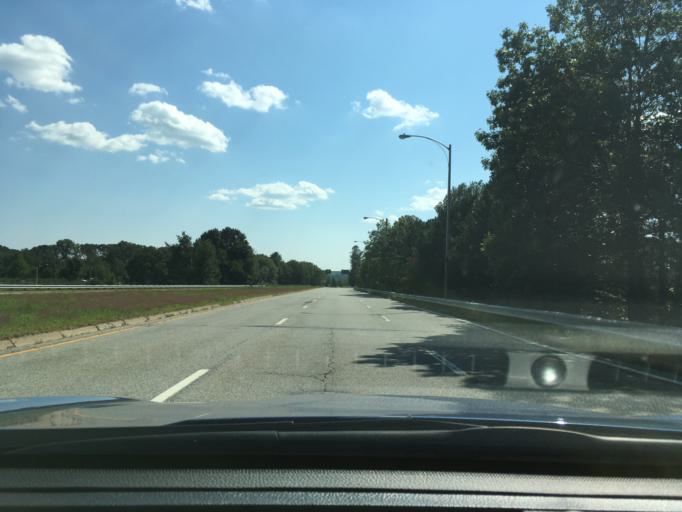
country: US
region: Rhode Island
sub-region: Providence County
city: Cranston
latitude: 41.7431
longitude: -71.4729
